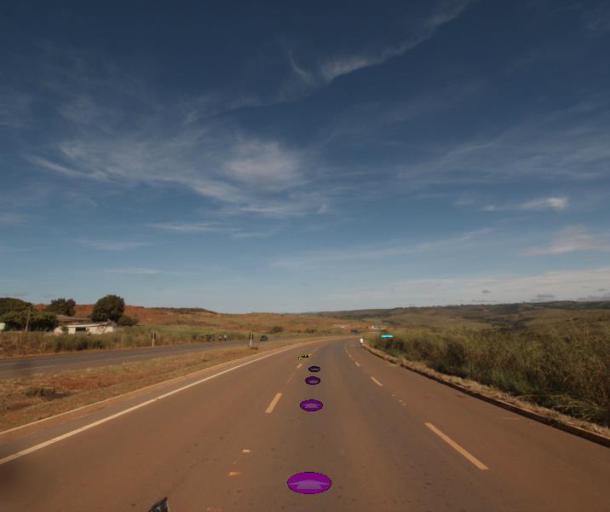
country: BR
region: Federal District
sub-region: Brasilia
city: Brasilia
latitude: -15.7556
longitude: -48.3317
